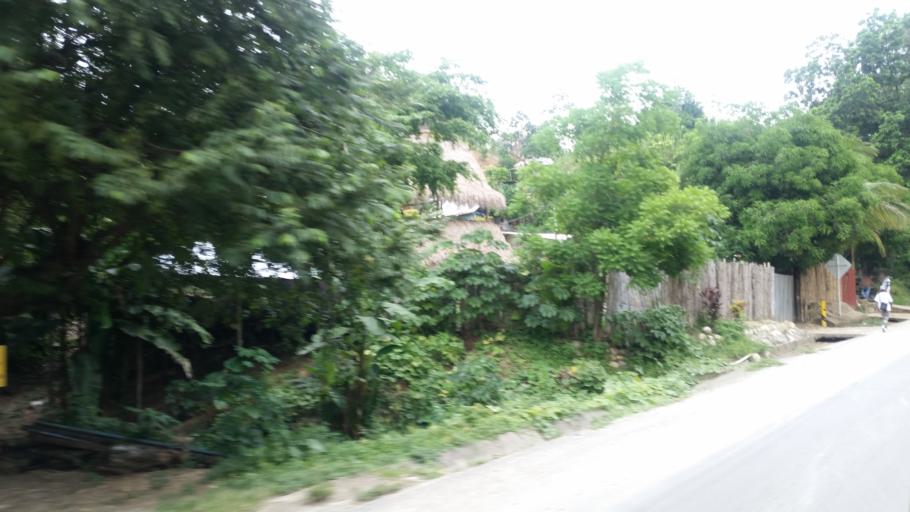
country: CO
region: Magdalena
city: Santa Marta
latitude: 11.2814
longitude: -73.9130
